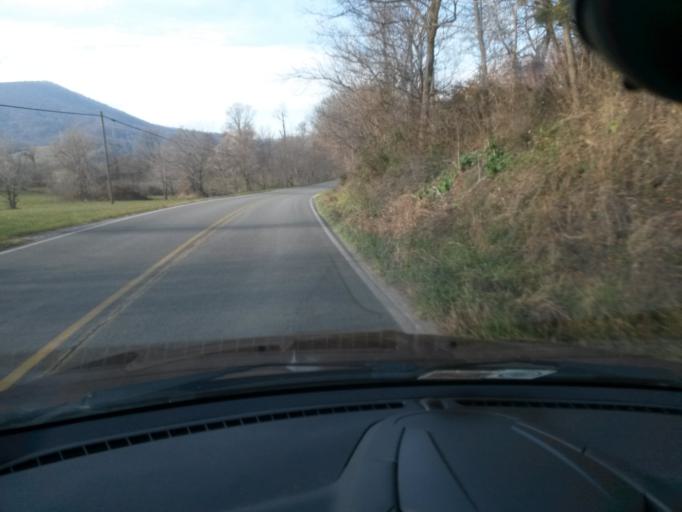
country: US
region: Virginia
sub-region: Botetourt County
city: Daleville
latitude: 37.4509
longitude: -79.9641
